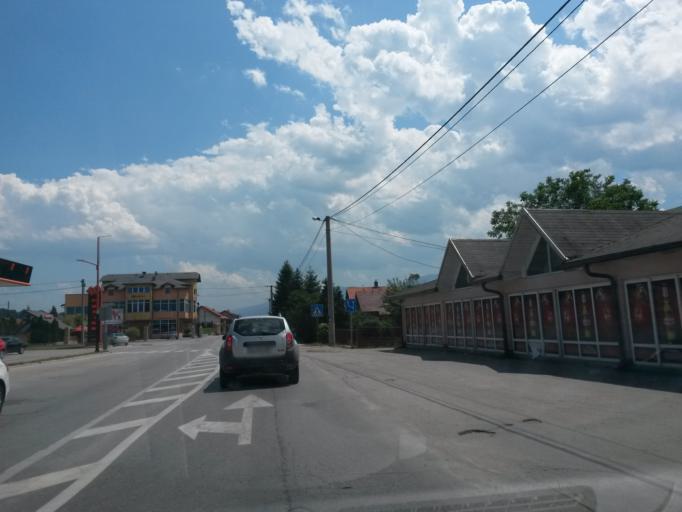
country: BA
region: Federation of Bosnia and Herzegovina
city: Vitez
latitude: 44.1827
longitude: 17.7502
